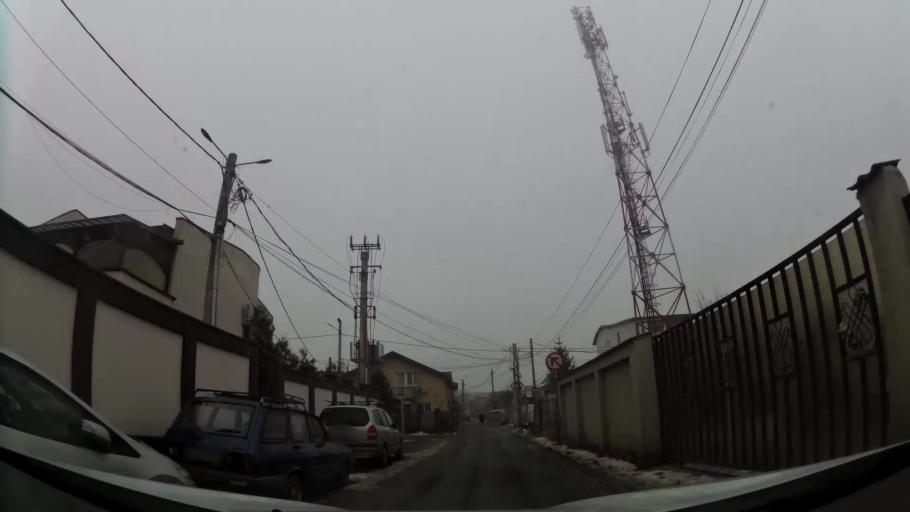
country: RO
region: Ilfov
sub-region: Comuna Chiajna
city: Rosu
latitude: 44.4473
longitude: 26.0099
